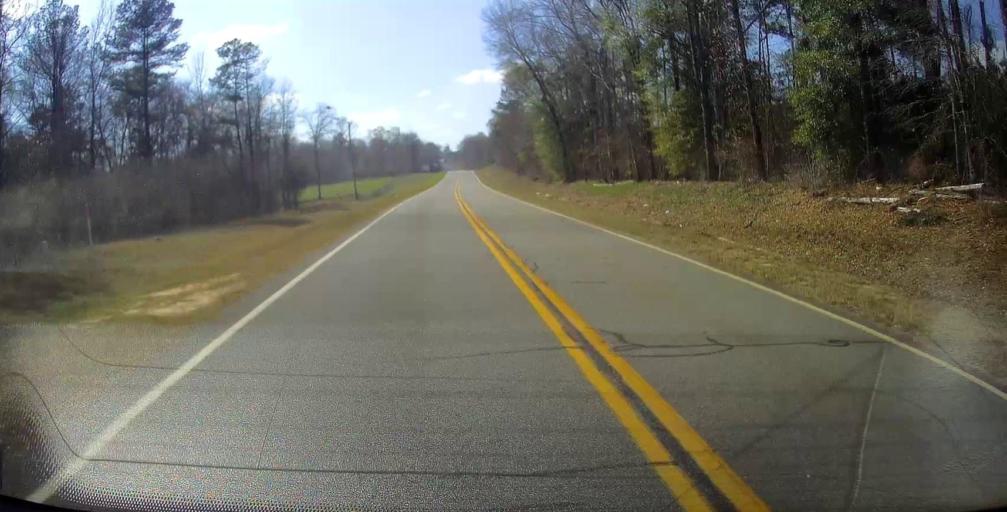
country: US
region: Georgia
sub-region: Twiggs County
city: Jeffersonville
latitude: 32.6812
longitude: -83.2814
